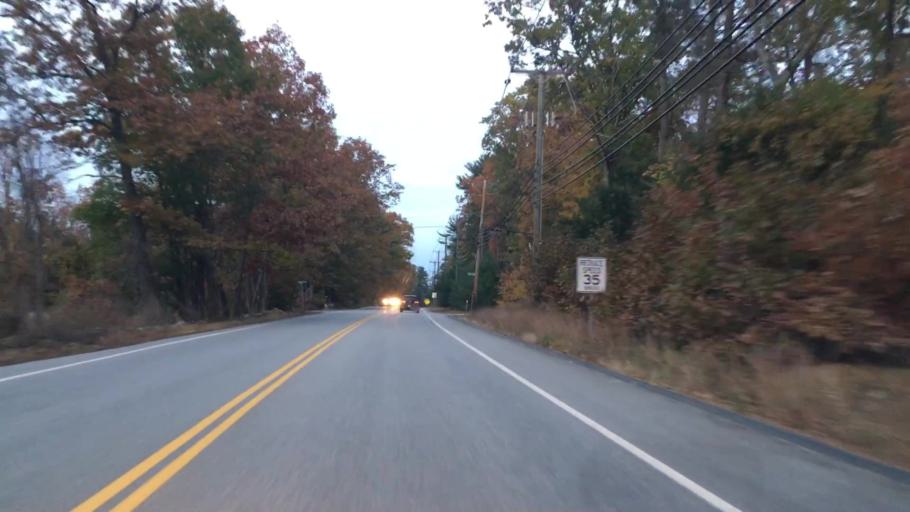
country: US
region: New Hampshire
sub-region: Hillsborough County
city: Milford
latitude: 42.8545
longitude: -71.6354
